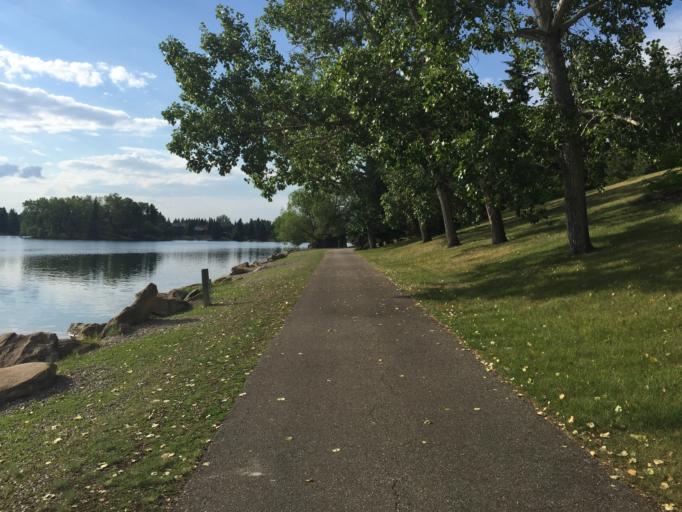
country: CA
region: Alberta
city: Calgary
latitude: 50.9395
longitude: -114.0502
